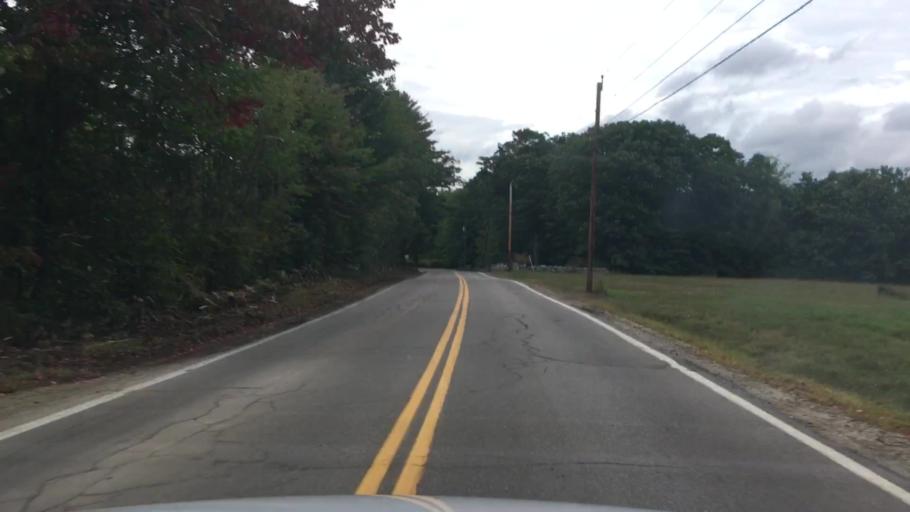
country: US
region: New Hampshire
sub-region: Carroll County
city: Effingham
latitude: 43.7682
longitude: -70.9971
